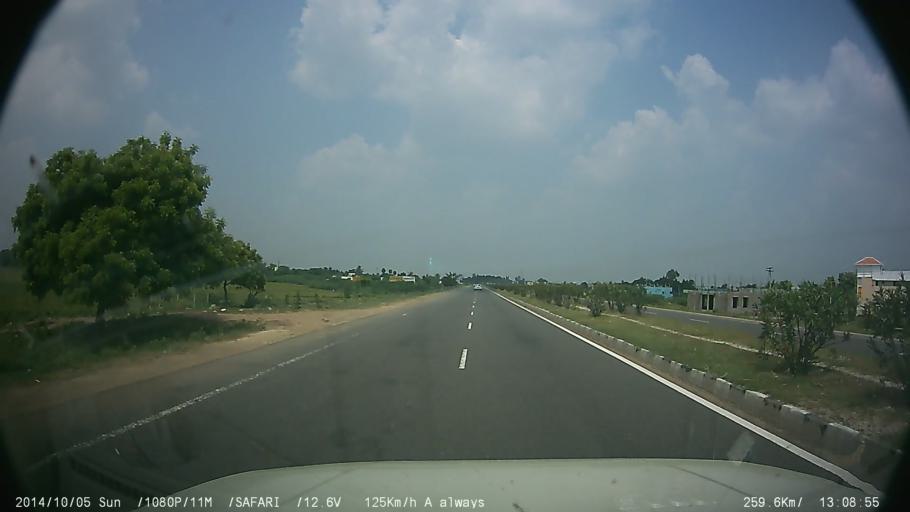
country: IN
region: Tamil Nadu
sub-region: Villupuram
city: Villupuram
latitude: 11.9216
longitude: 79.4717
